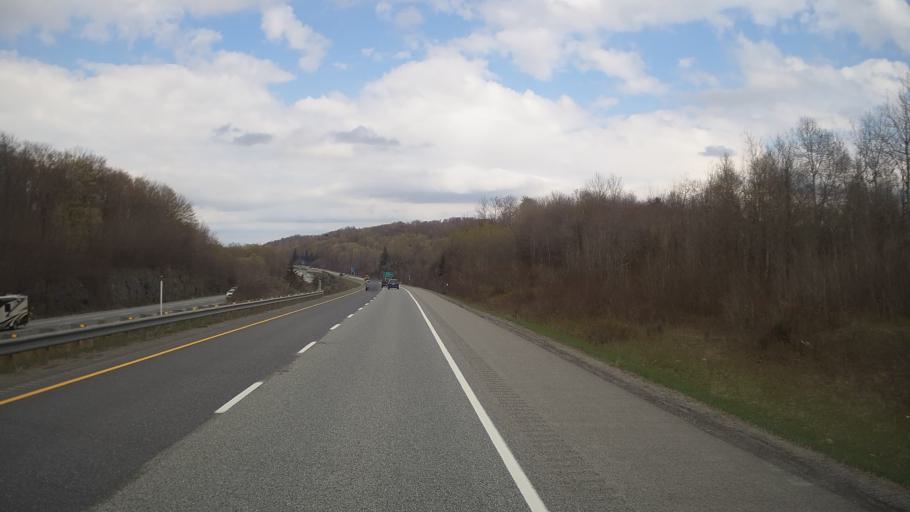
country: CA
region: Quebec
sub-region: Estrie
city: Magog
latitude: 45.2894
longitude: -72.2604
